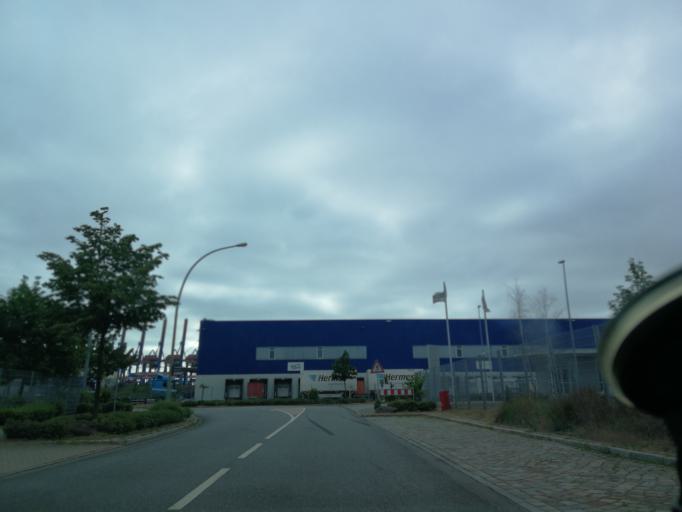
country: DE
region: Hamburg
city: Altona
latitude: 53.5035
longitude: 9.9250
